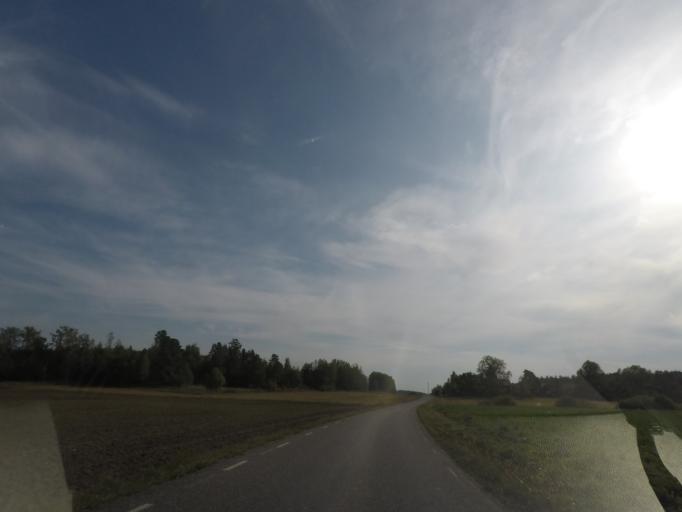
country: SE
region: Vaestmanland
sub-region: Kungsors Kommun
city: Kungsoer
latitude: 59.5173
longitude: 16.1480
